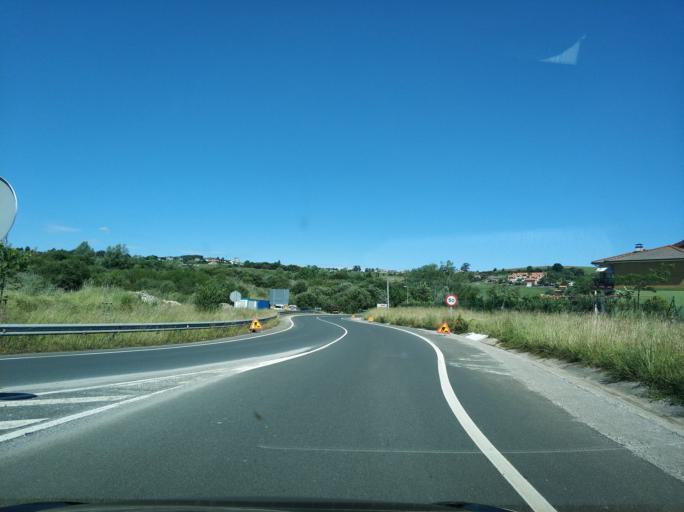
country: ES
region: Cantabria
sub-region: Provincia de Cantabria
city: Camargo
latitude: 43.3856
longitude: -3.8574
